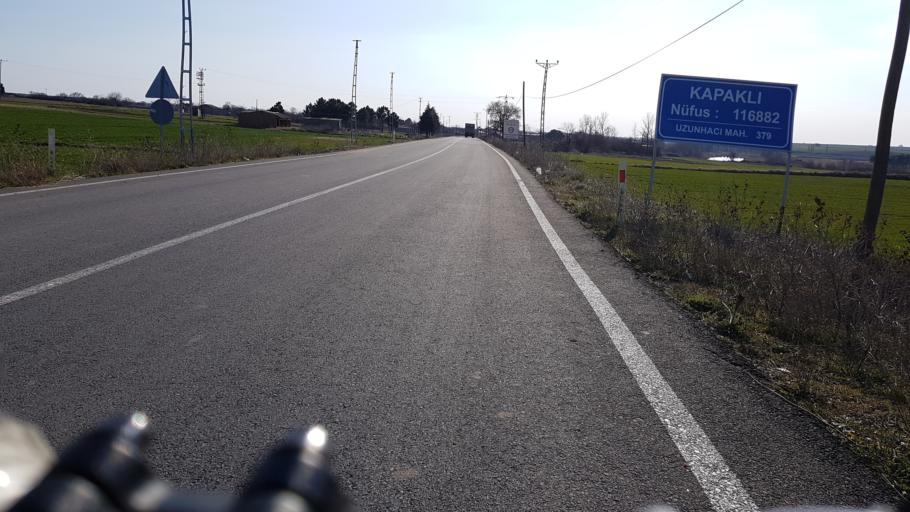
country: TR
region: Tekirdag
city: Velimese
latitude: 41.3499
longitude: 27.8390
